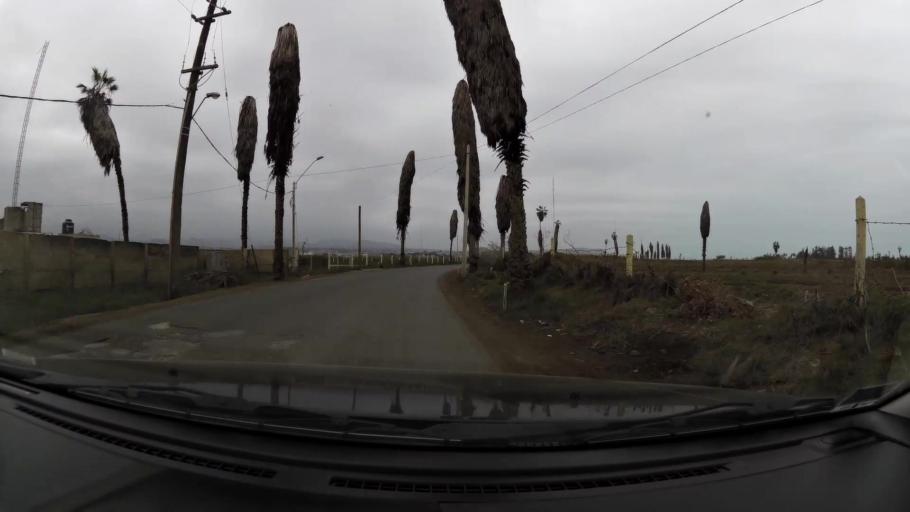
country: PE
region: Lima
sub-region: Lima
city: Surco
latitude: -12.2086
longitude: -76.9989
